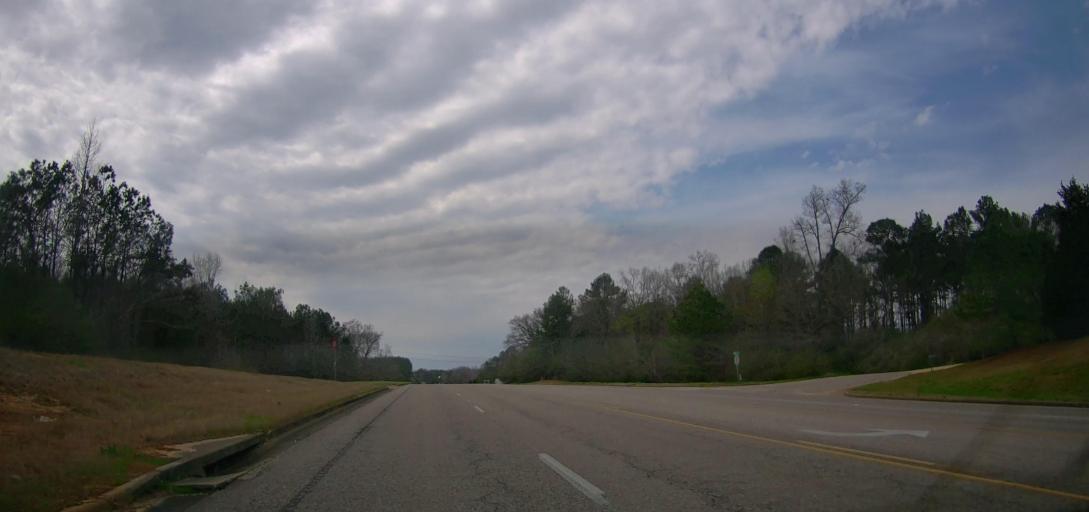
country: US
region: Alabama
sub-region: Marion County
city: Winfield
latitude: 33.9472
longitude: -87.8575
